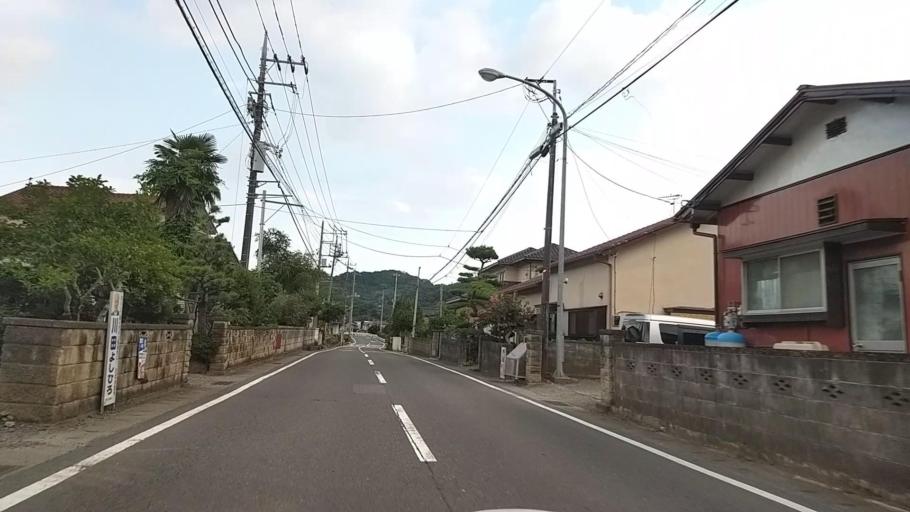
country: JP
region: Yamanashi
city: Uenohara
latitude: 35.6177
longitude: 139.1272
